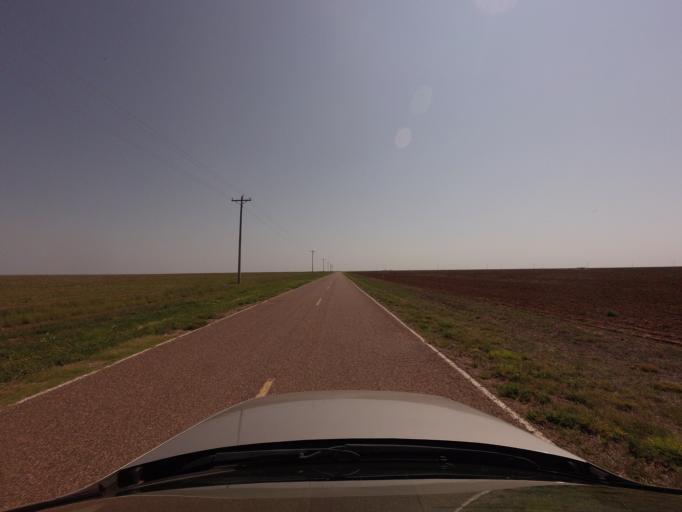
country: US
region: New Mexico
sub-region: Curry County
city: Cannon Air Force Base
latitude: 34.6327
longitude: -103.3073
